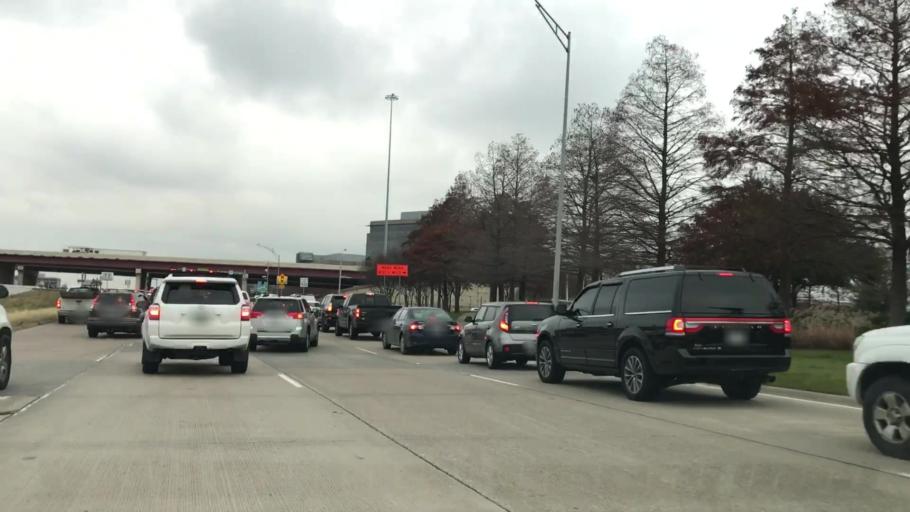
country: US
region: Texas
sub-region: Dallas County
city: Coppell
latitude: 32.8951
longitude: -96.9696
